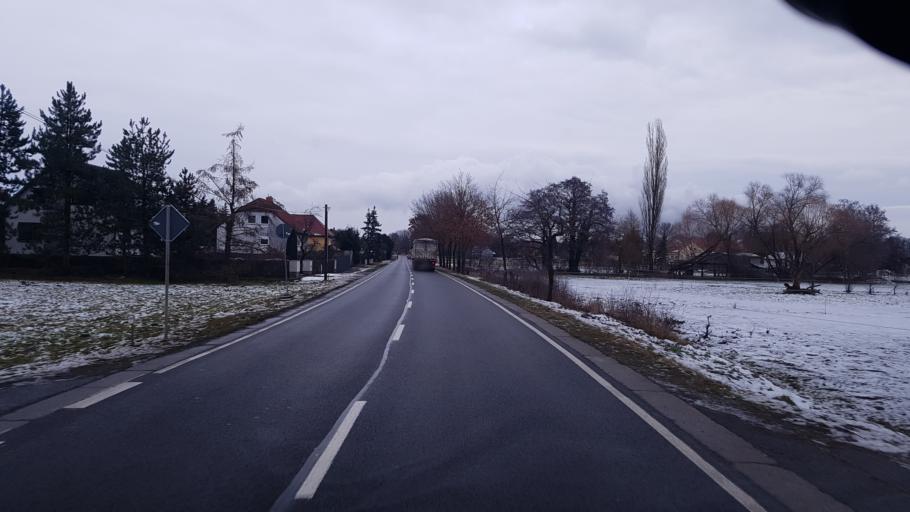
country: DE
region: Brandenburg
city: Peitz
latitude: 51.8496
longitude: 14.4172
